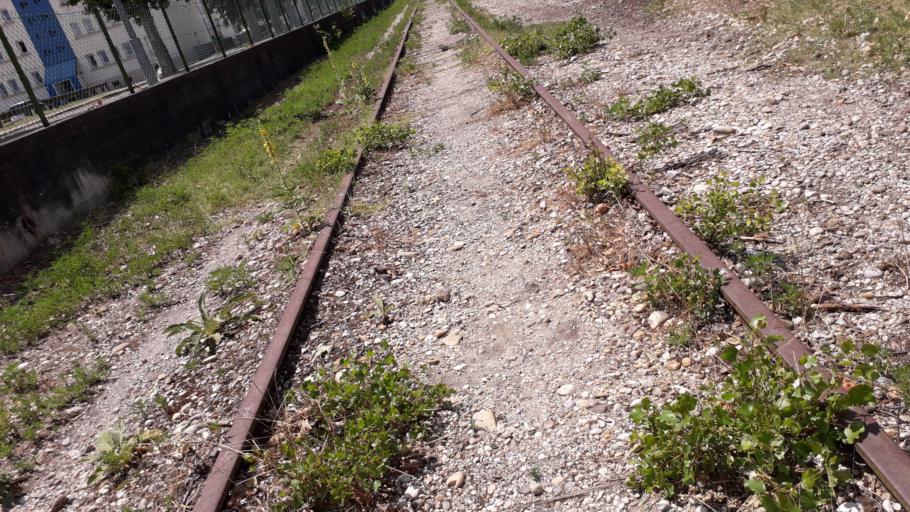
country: FR
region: Rhone-Alpes
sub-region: Departement de l'Isere
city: Charvieu-Chavagneux
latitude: 45.7469
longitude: 5.1663
